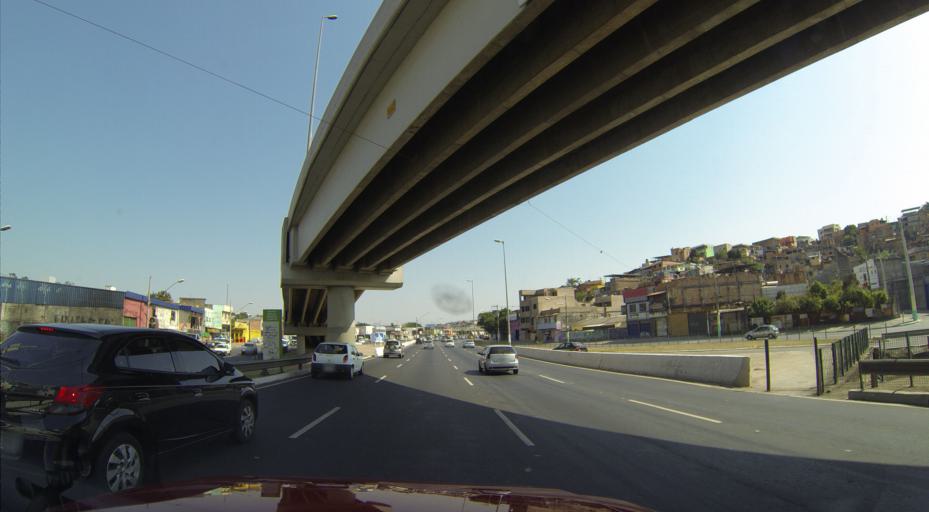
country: BR
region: Minas Gerais
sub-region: Belo Horizonte
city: Belo Horizonte
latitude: -19.8637
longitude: -43.9317
